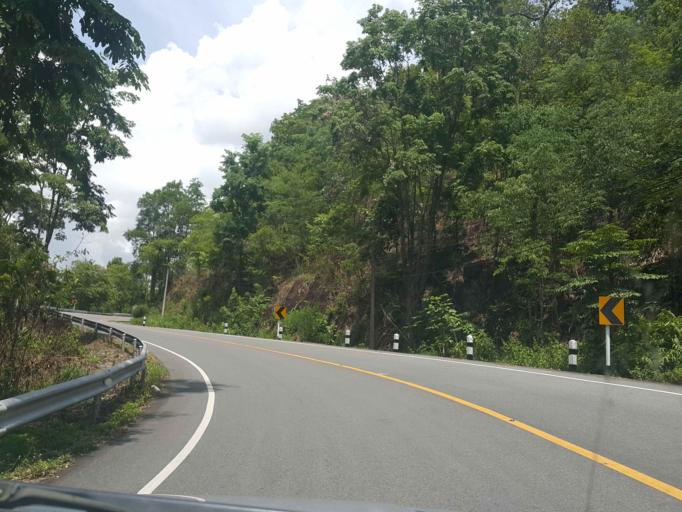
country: TH
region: Phayao
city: Chiang Muan
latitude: 18.8492
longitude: 100.3317
